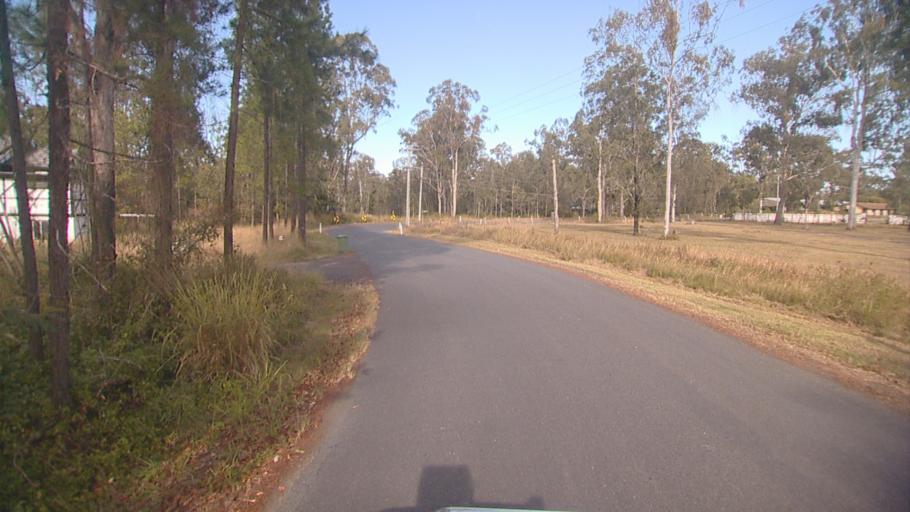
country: AU
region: Queensland
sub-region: Logan
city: Park Ridge South
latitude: -27.7473
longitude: 153.0352
